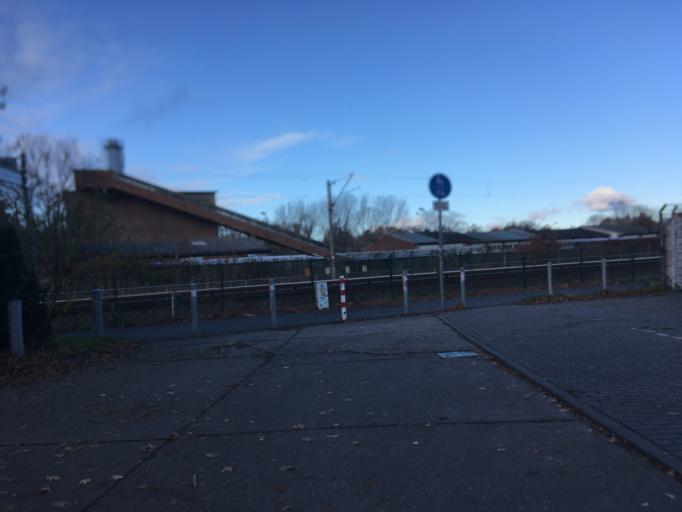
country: DE
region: Berlin
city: Karlshorst
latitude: 52.4956
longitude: 13.5323
